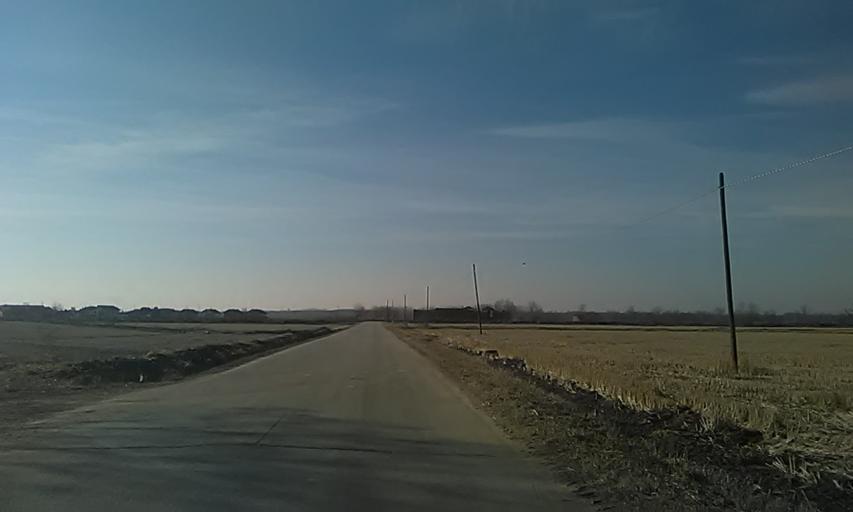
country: IT
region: Piedmont
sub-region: Provincia di Vercelli
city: Balocco
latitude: 45.4626
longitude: 8.2820
